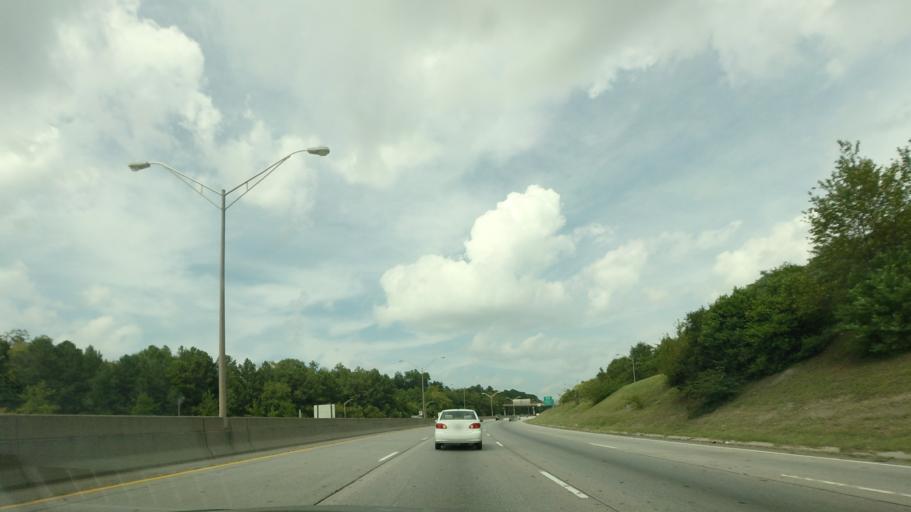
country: US
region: Georgia
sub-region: Bibb County
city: Macon
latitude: 32.8270
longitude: -83.6567
